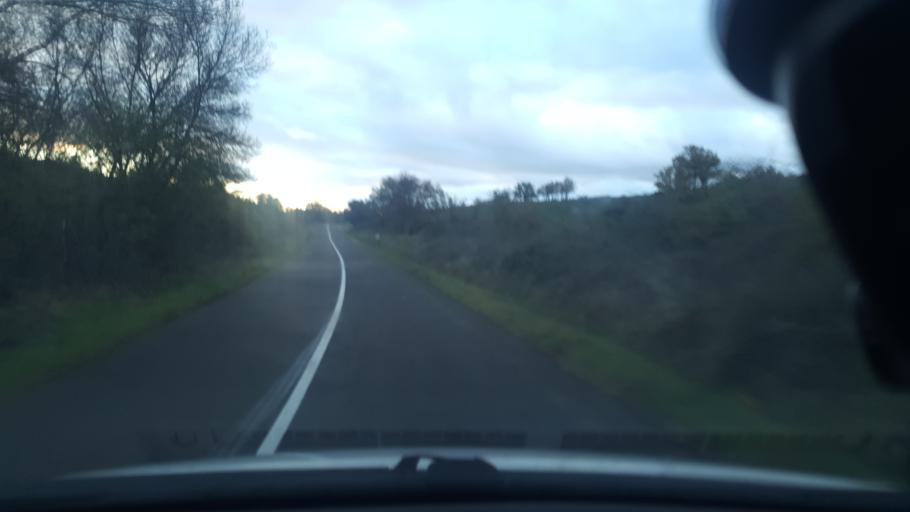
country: ES
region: Castille and Leon
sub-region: Provincia de Segovia
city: Vegas de Matute
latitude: 40.7265
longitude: -4.2884
